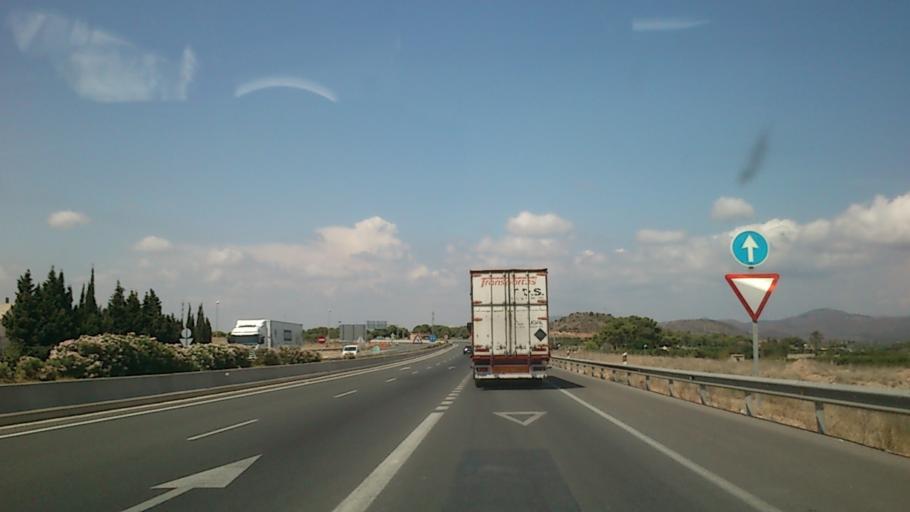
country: ES
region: Valencia
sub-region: Provincia de Valencia
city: Museros
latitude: 39.5906
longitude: -0.3581
